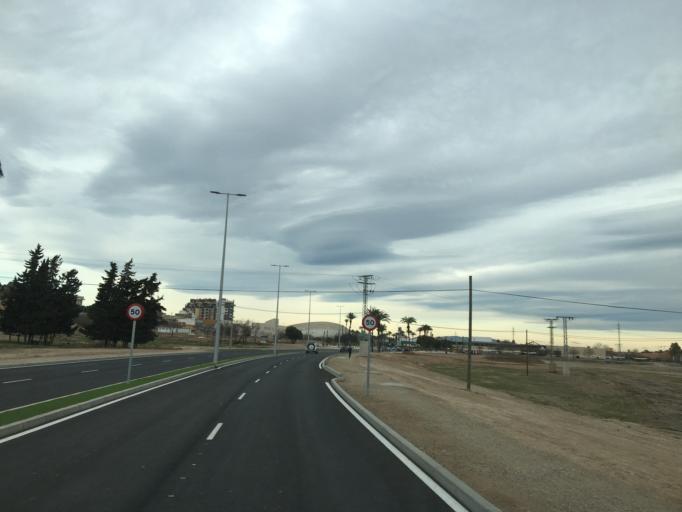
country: ES
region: Murcia
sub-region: Murcia
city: Cartagena
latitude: 37.6096
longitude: -1.0012
